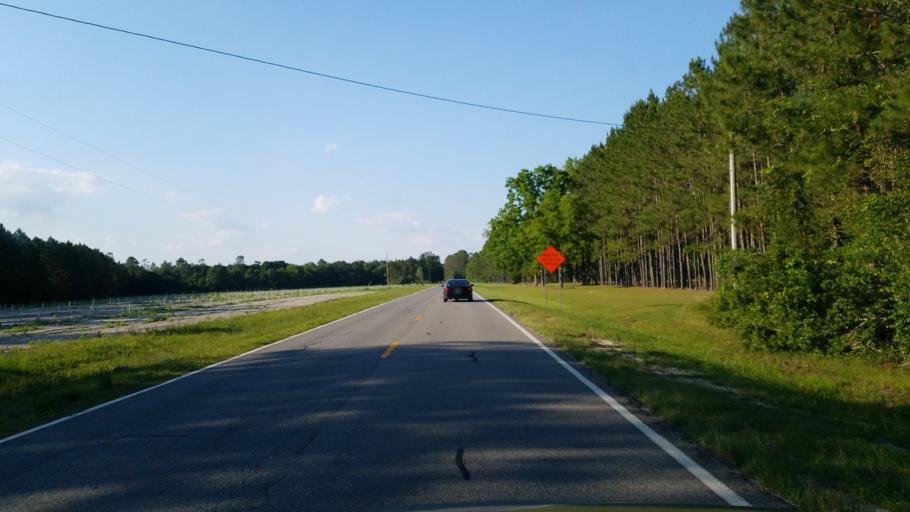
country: US
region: Georgia
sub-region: Lanier County
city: Lakeland
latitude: 30.9867
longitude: -83.0719
